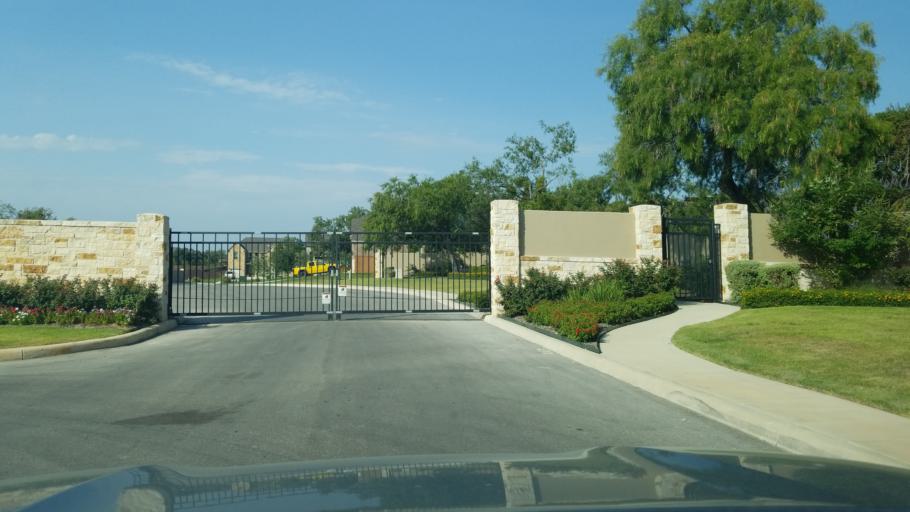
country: US
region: Texas
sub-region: Bexar County
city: Helotes
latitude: 29.4640
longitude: -98.7629
